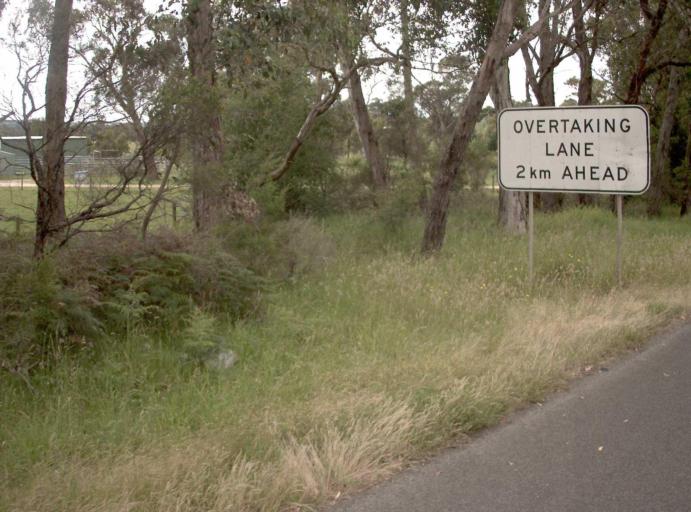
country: AU
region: Victoria
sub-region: Cardinia
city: Koo-Wee-Rup
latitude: -38.3547
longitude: 145.6498
